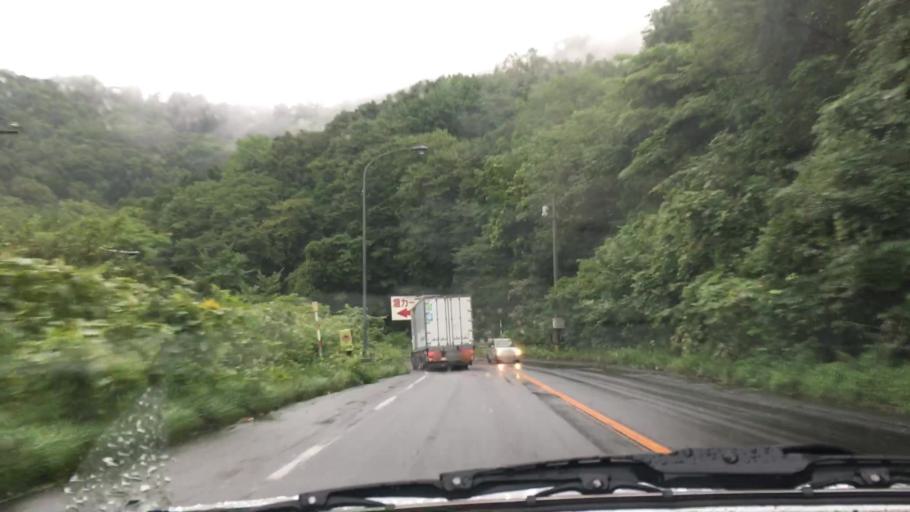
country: JP
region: Hokkaido
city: Niseko Town
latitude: 42.5937
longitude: 140.5929
